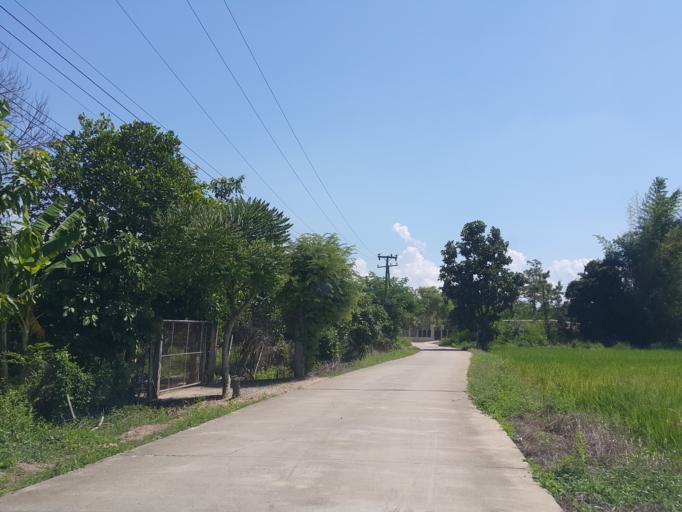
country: TH
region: Chiang Mai
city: Saraphi
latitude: 18.7626
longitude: 99.0585
